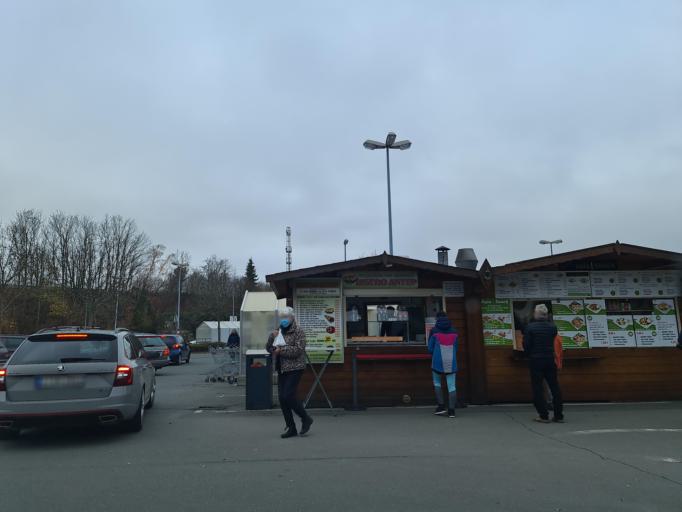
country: DE
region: Saxony
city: Plauen
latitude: 50.5144
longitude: 12.1255
